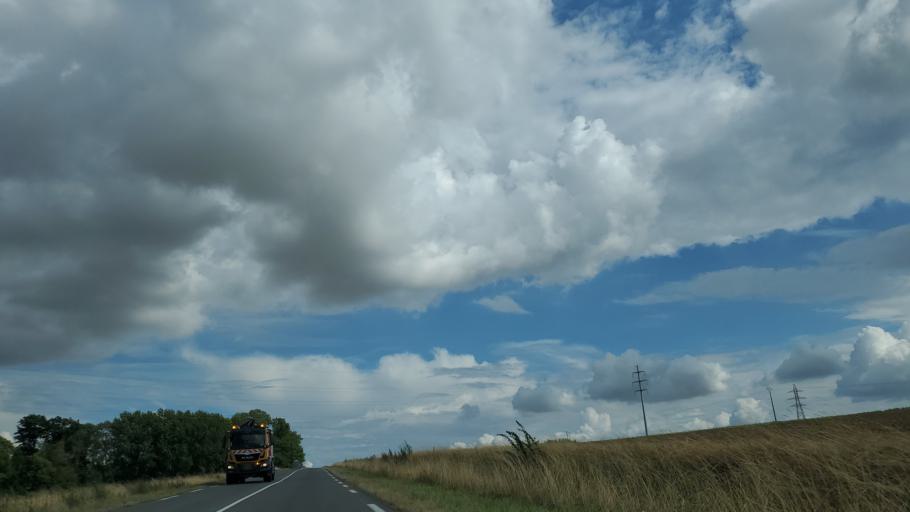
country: FR
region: Ile-de-France
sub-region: Departement de Seine-et-Marne
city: Coulommiers
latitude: 48.7970
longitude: 3.0977
